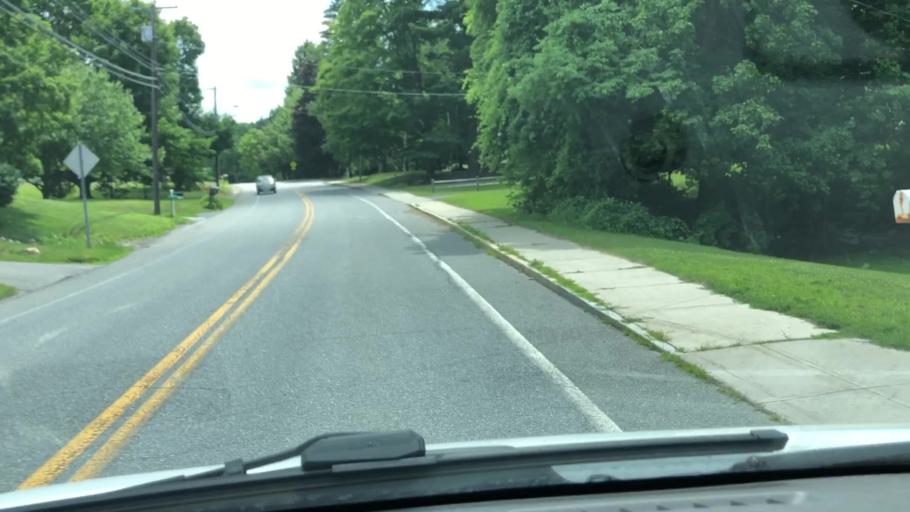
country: US
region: Massachusetts
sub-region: Berkshire County
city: Adams
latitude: 42.6103
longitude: -73.1187
